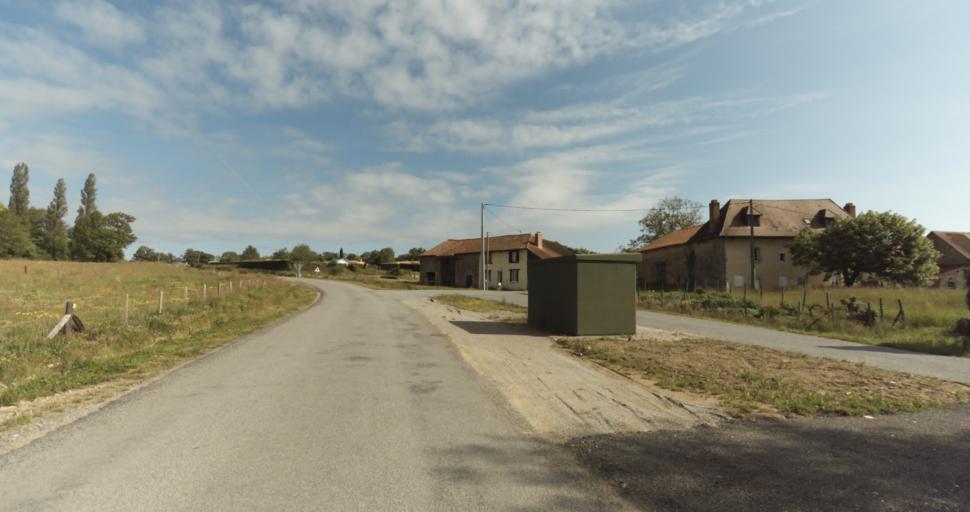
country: FR
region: Limousin
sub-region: Departement de la Haute-Vienne
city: Bosmie-l'Aiguille
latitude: 45.7073
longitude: 1.2409
